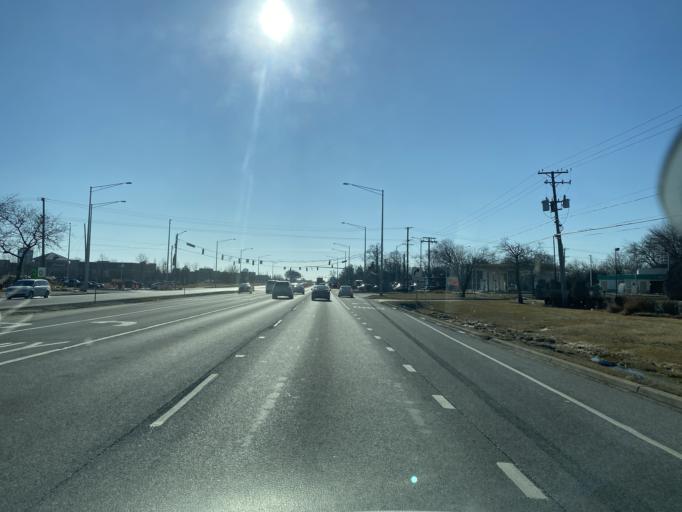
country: US
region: Illinois
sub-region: DuPage County
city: Willowbrook
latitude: 41.7620
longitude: -87.9451
